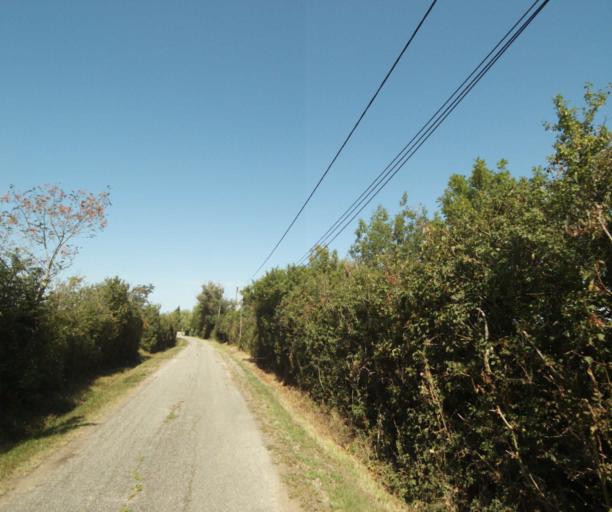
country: FR
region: Midi-Pyrenees
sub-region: Departement de l'Ariege
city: Lezat-sur-Leze
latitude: 43.2476
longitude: 1.3827
